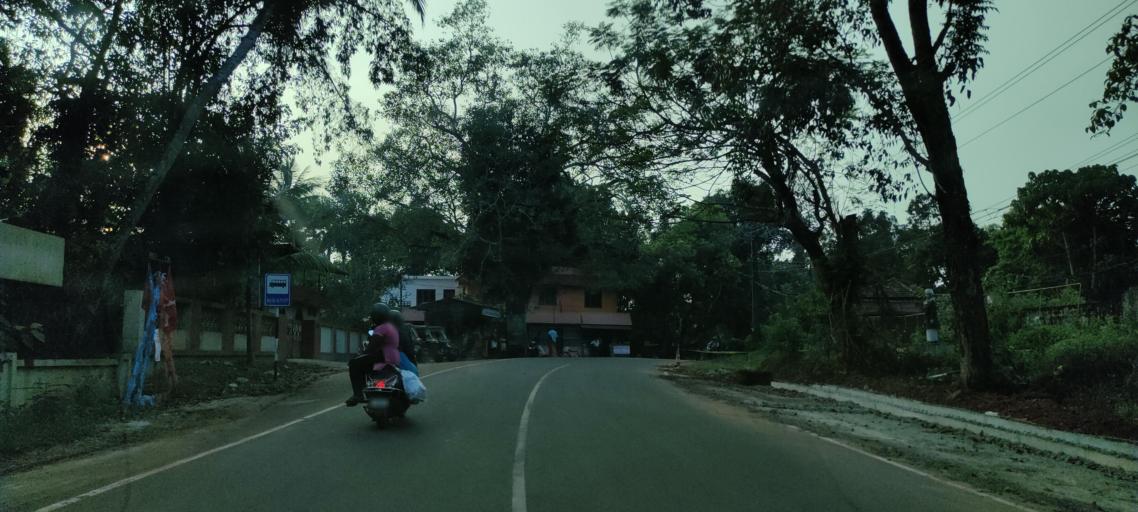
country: IN
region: Kerala
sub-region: Alappuzha
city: Mavelikara
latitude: 9.2505
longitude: 76.5700
